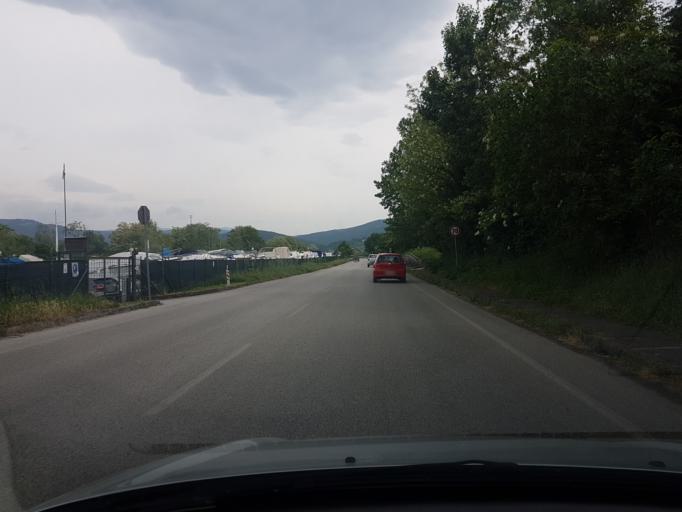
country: SI
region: Koper-Capodistria
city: Spodnje Skofije
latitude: 45.5943
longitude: 13.7904
